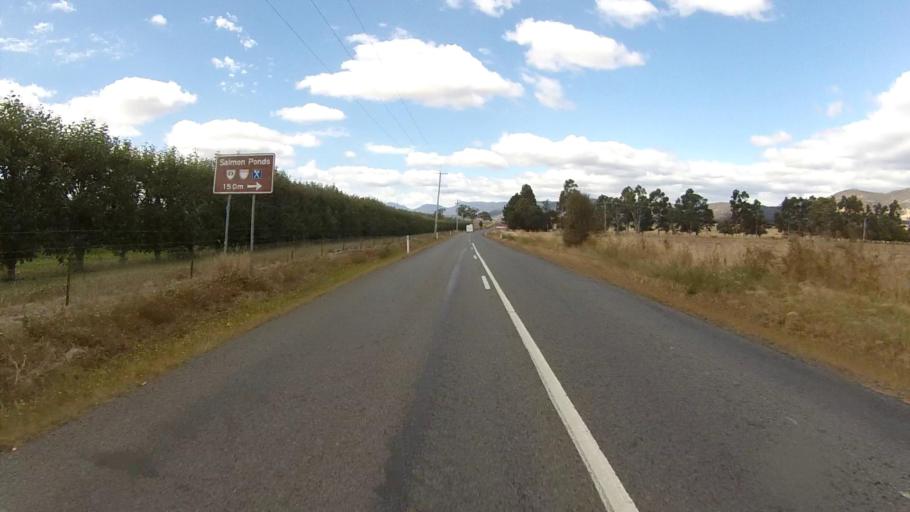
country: AU
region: Tasmania
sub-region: Derwent Valley
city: New Norfolk
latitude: -42.7482
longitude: 146.9730
